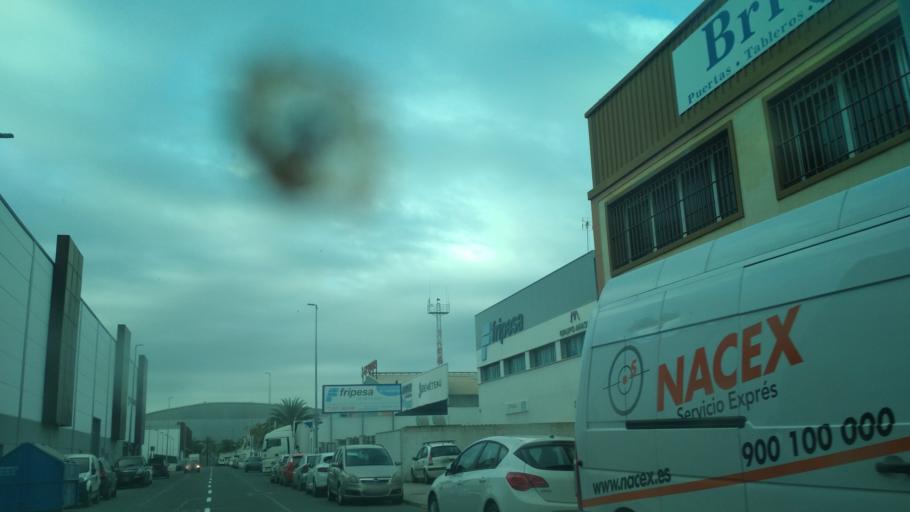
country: ES
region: Andalusia
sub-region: Provincia de Huelva
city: Huelva
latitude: 37.2649
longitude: -6.9594
